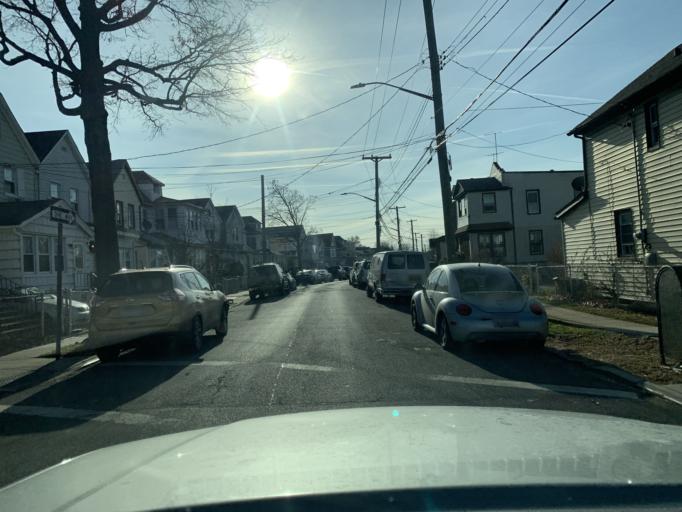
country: US
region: New York
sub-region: Queens County
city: Jamaica
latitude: 40.7018
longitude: -73.7864
